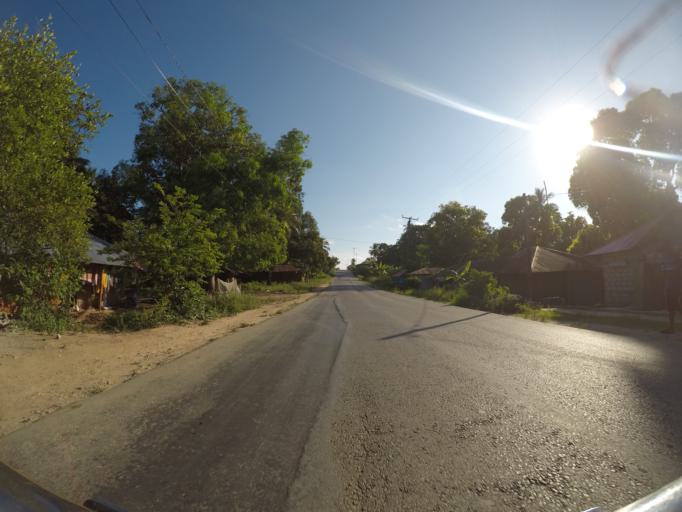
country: TZ
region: Pemba South
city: Chake Chake
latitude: -5.2912
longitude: 39.7608
